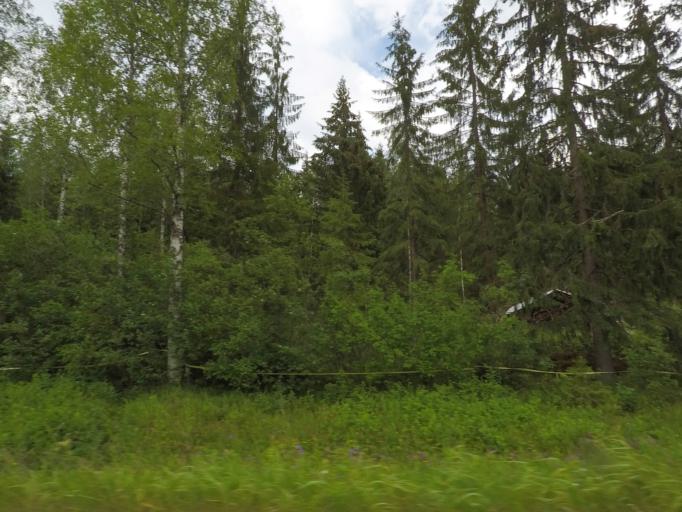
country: FI
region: Paijanne Tavastia
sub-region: Lahti
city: Hollola
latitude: 60.8348
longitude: 25.4920
